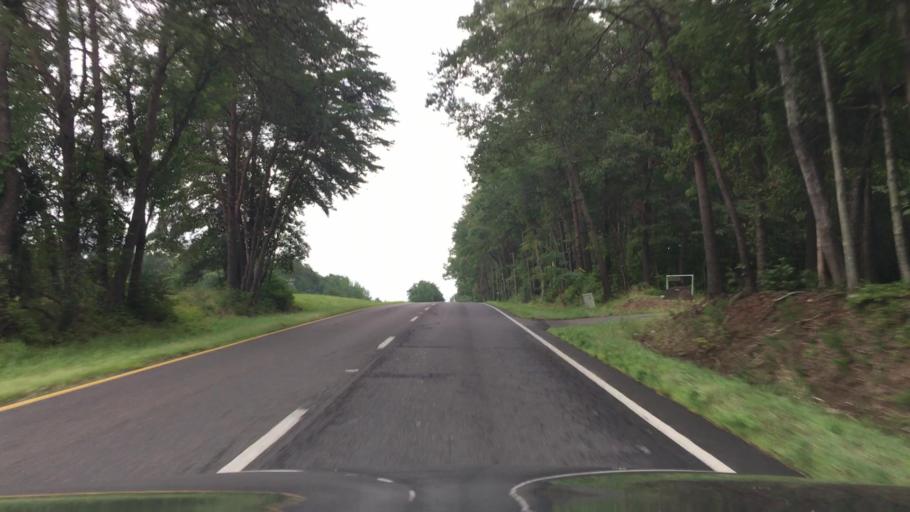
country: US
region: Virginia
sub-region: Spotsylvania County
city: Spotsylvania
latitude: 38.3209
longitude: -77.7001
